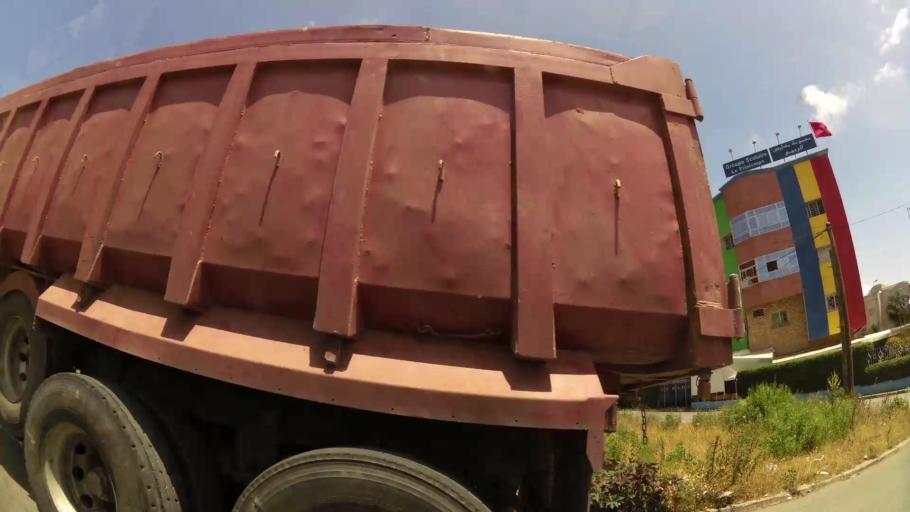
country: MA
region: Gharb-Chrarda-Beni Hssen
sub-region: Kenitra Province
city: Kenitra
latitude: 34.2508
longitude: -6.6145
